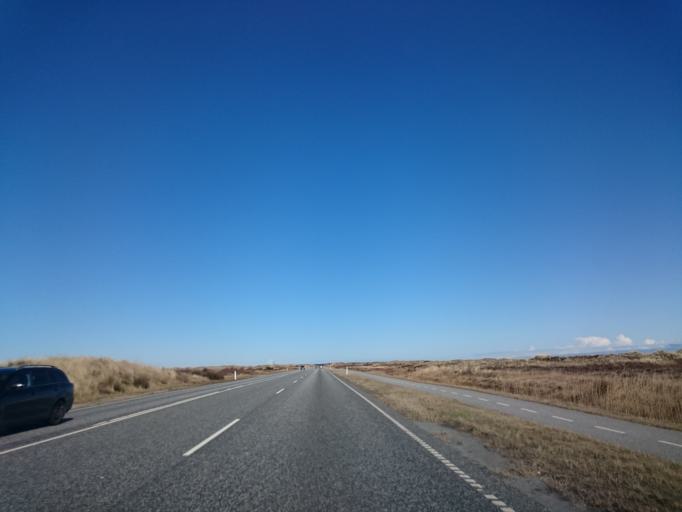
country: DK
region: North Denmark
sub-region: Frederikshavn Kommune
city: Skagen
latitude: 57.6766
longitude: 10.4590
